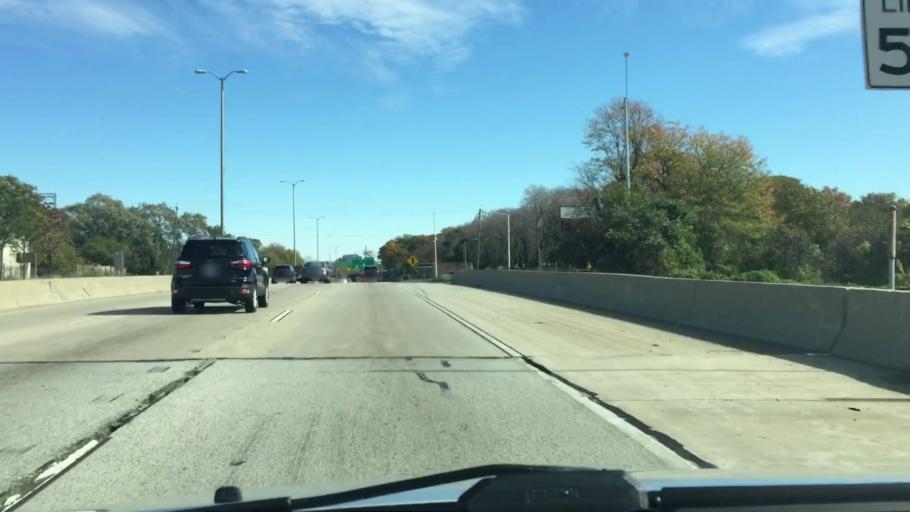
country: US
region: Wisconsin
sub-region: Milwaukee County
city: West Milwaukee
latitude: 43.0308
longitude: -87.9869
